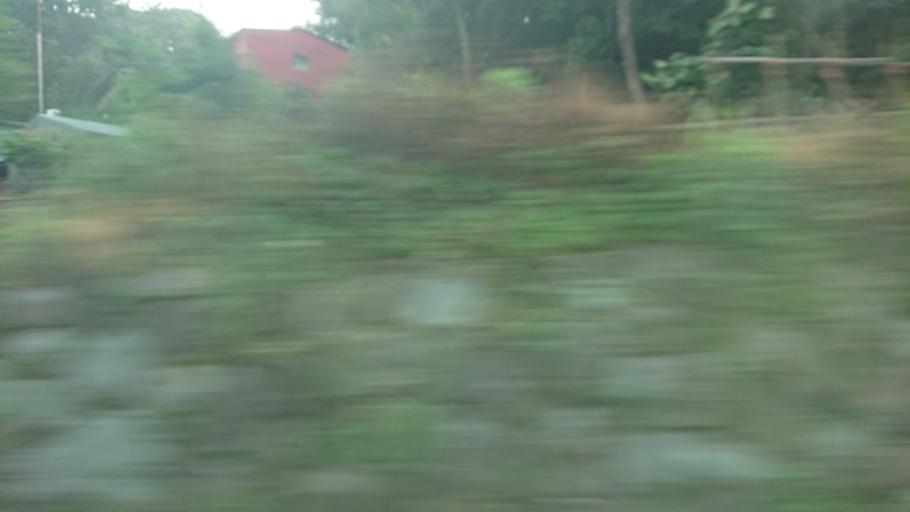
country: TW
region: Taiwan
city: Daxi
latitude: 24.8935
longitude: 121.3756
